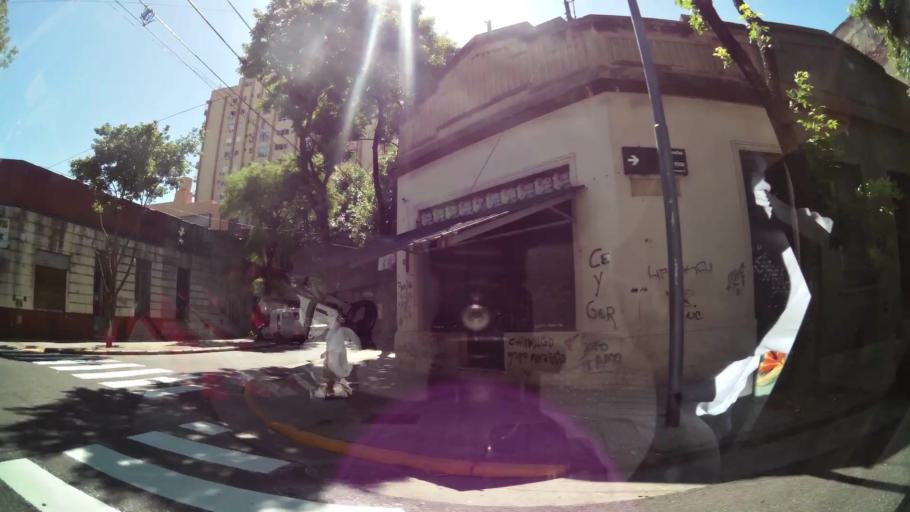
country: AR
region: Buenos Aires F.D.
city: Buenos Aires
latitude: -34.6259
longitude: -58.3972
